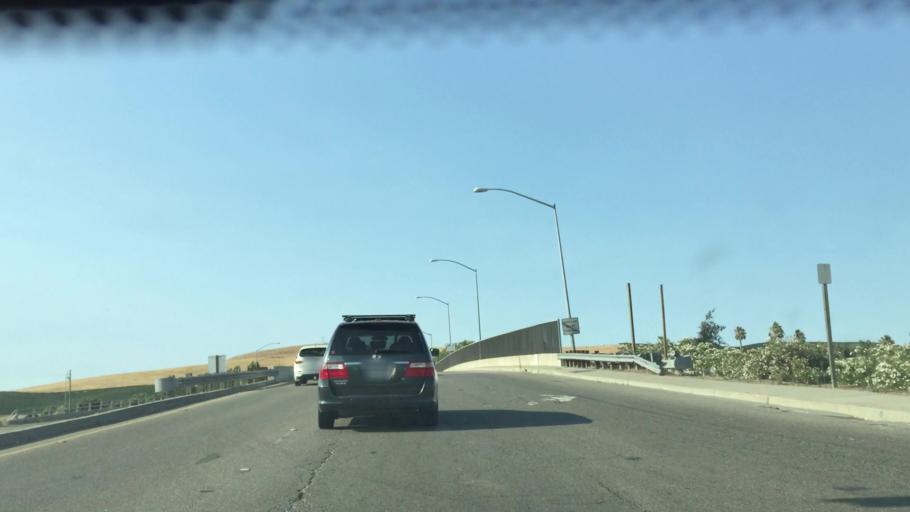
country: US
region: California
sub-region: Alameda County
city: Livermore
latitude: 37.7000
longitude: -121.8178
